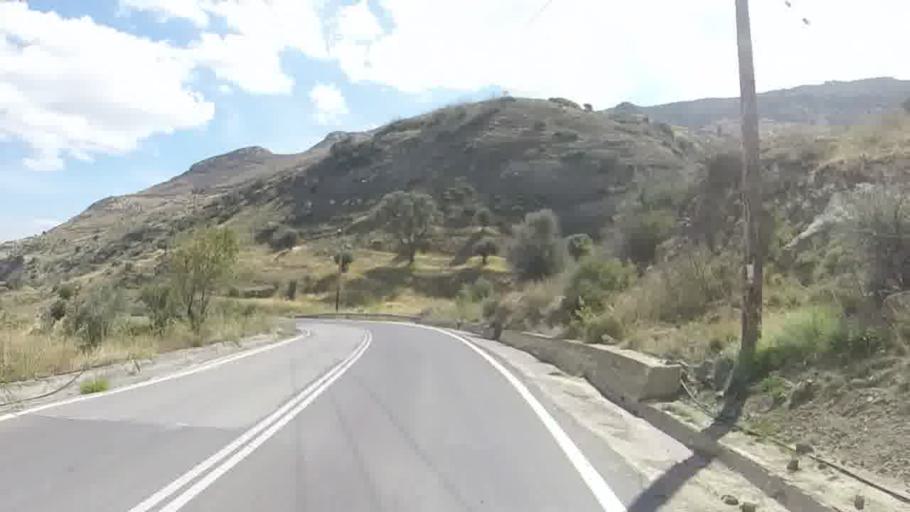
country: GR
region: Crete
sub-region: Nomos Rethymnis
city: Agia Galini
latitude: 35.1429
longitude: 24.6351
